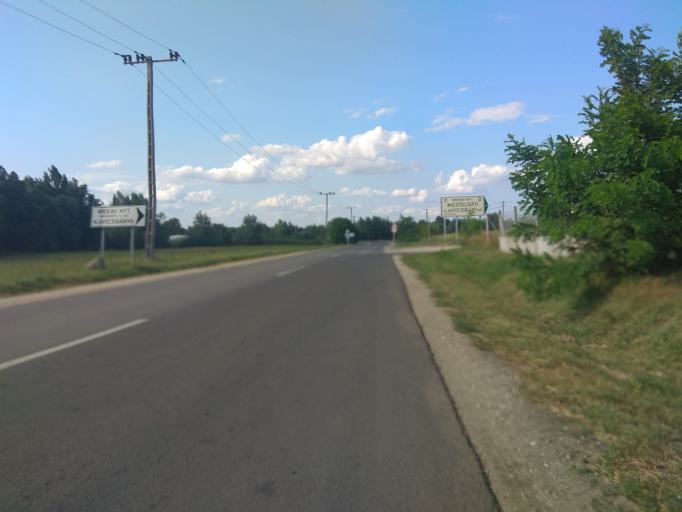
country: HU
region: Borsod-Abauj-Zemplen
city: Mezocsat
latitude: 47.8368
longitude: 20.9004
